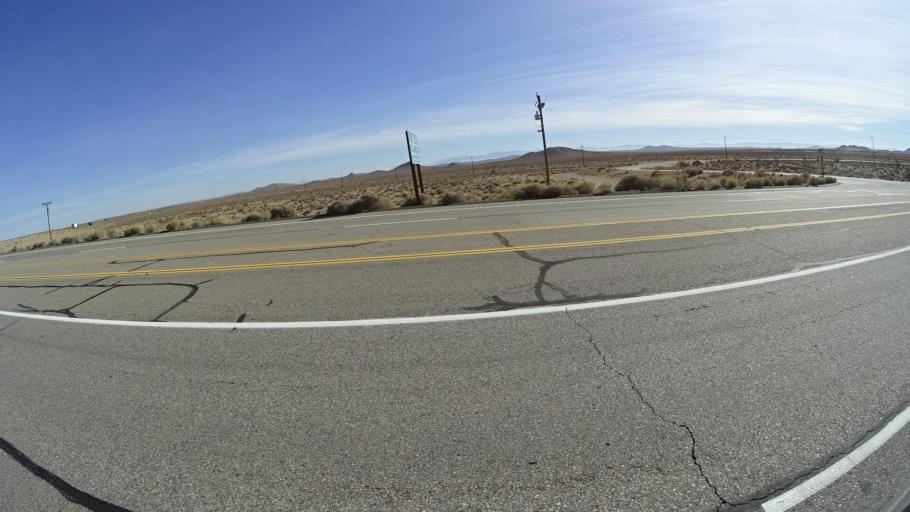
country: US
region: California
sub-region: Kern County
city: Mojave
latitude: 35.0363
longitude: -118.1111
